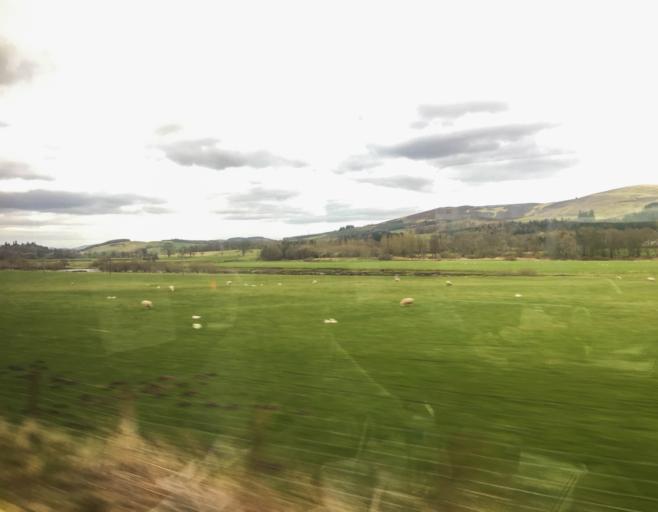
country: GB
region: Scotland
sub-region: South Lanarkshire
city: Biggar
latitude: 55.5637
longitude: -3.6310
